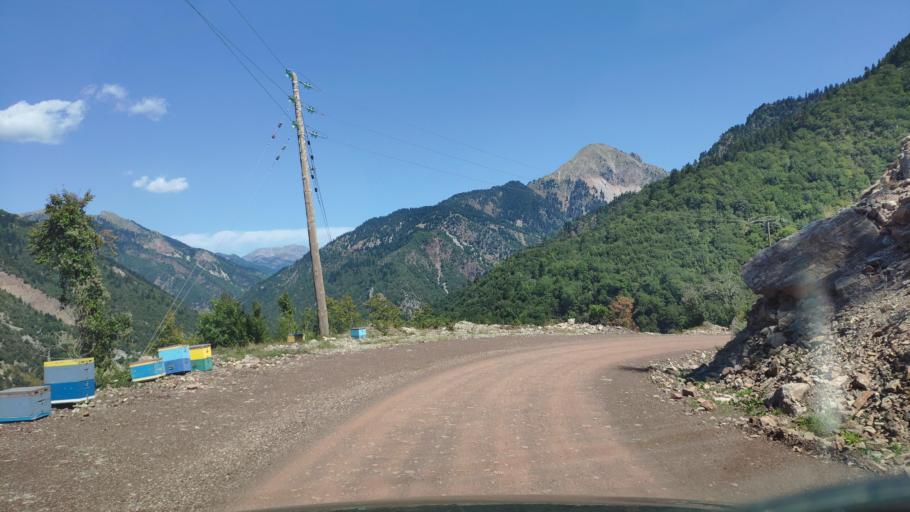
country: GR
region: Central Greece
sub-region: Nomos Evrytanias
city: Kerasochori
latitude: 39.1154
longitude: 21.6241
